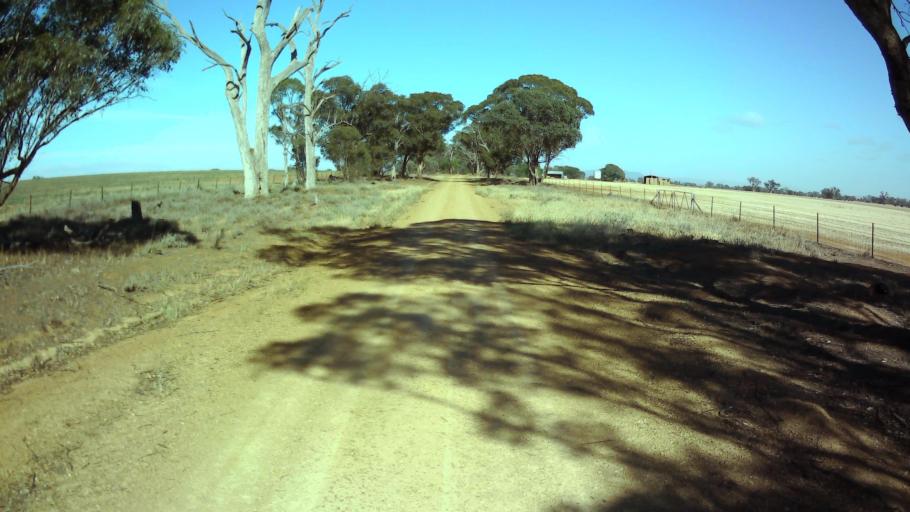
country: AU
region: New South Wales
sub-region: Weddin
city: Grenfell
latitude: -34.0478
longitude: 148.2822
